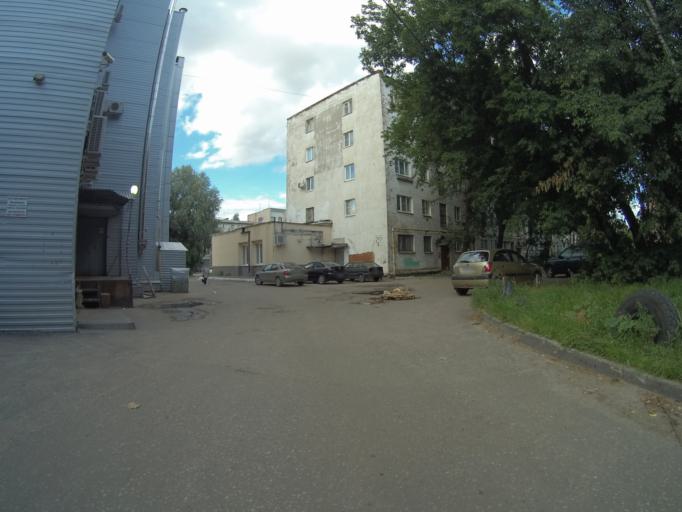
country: RU
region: Vladimir
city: Vladimir
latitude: 56.1192
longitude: 40.3670
